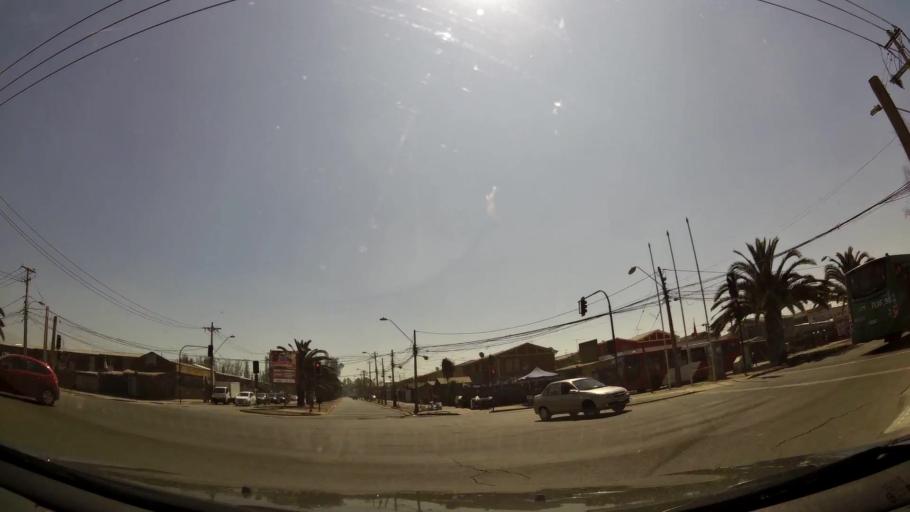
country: CL
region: Santiago Metropolitan
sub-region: Provincia de Santiago
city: Lo Prado
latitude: -33.3619
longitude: -70.7538
